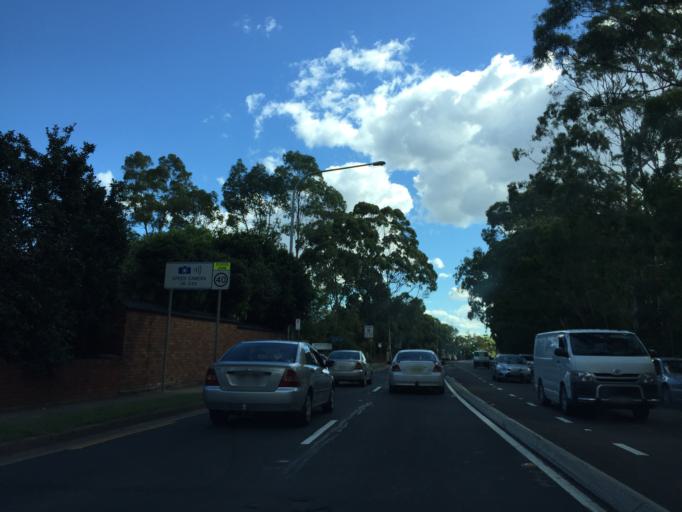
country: AU
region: New South Wales
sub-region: Parramatta
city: Telopea
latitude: -33.7924
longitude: 151.0201
